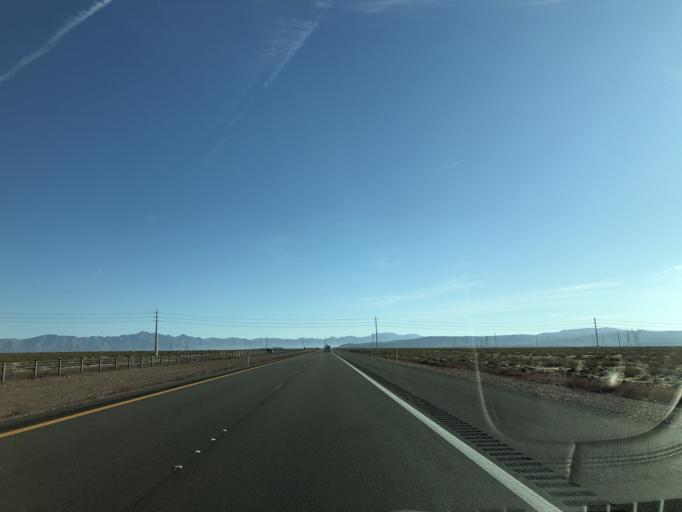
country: US
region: Nevada
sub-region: Clark County
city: Boulder City
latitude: 35.9344
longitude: -114.8334
